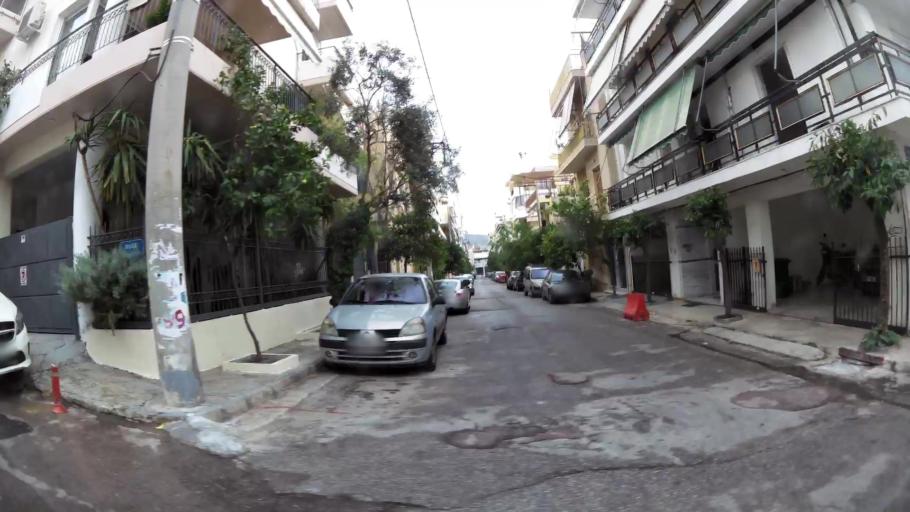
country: GR
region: Attica
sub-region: Nomarchia Athinas
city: Kaisariani
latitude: 37.9591
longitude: 23.7650
